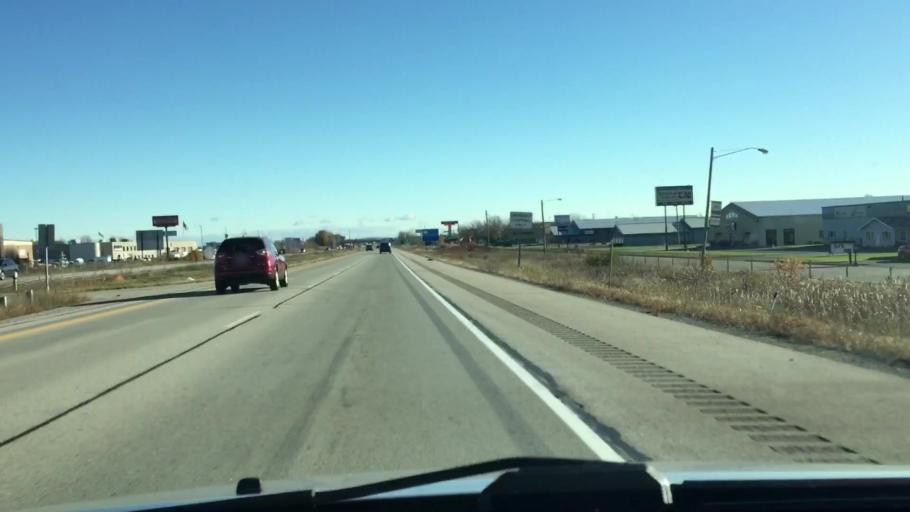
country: US
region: Wisconsin
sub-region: Outagamie County
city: Kaukauna
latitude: 44.3022
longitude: -88.2614
